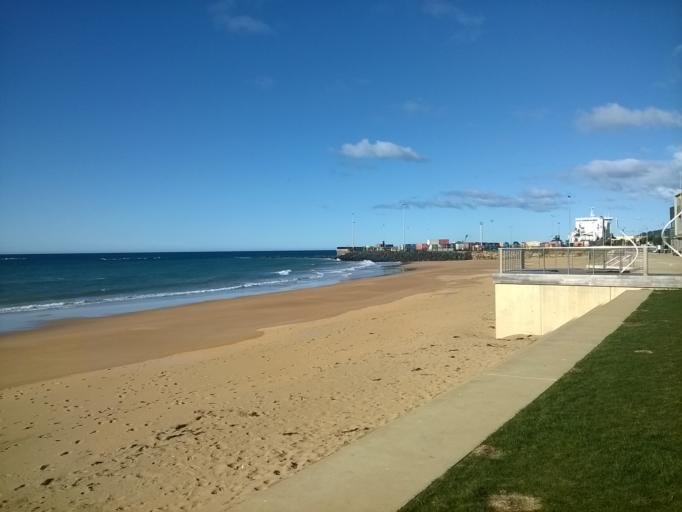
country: AU
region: Tasmania
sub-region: Burnie
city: Burnie
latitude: -41.0491
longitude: 145.9052
